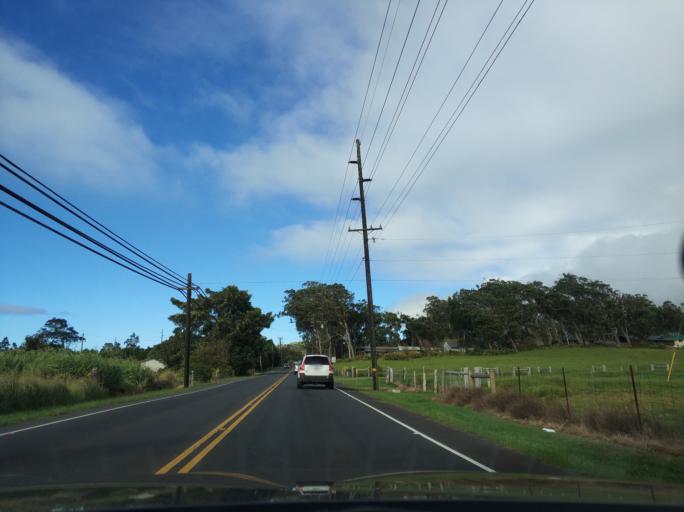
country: US
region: Hawaii
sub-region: Hawaii County
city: Waimea
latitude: 20.0354
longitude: -155.6300
